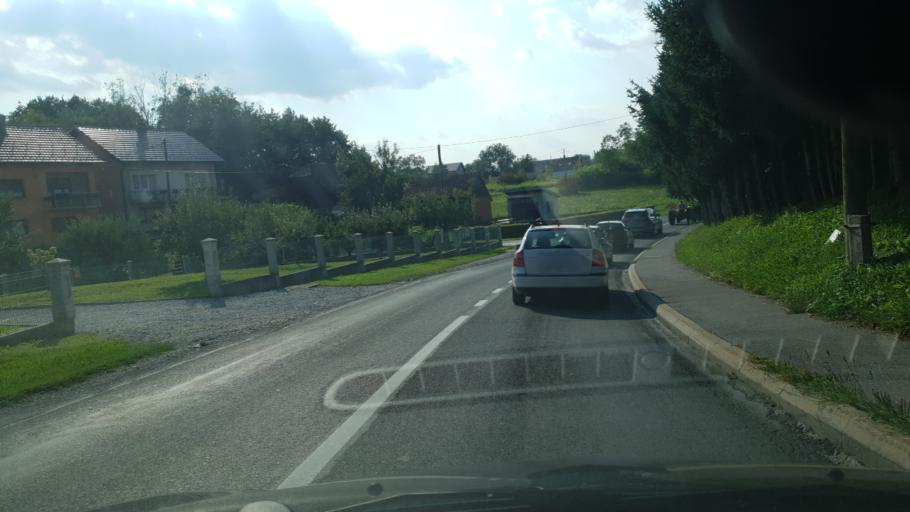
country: HR
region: Krapinsko-Zagorska
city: Oroslavje
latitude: 45.9850
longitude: 15.9207
